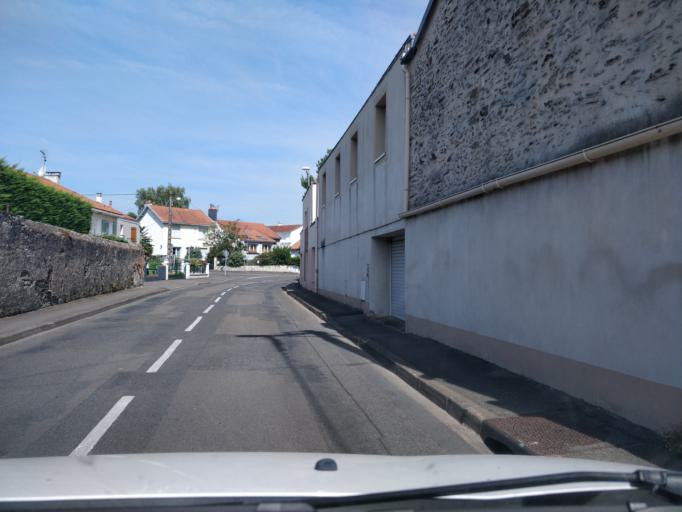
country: FR
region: Pays de la Loire
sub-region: Departement de la Loire-Atlantique
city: Saint-Sebastien-sur-Loire
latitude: 47.2063
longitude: -1.4986
